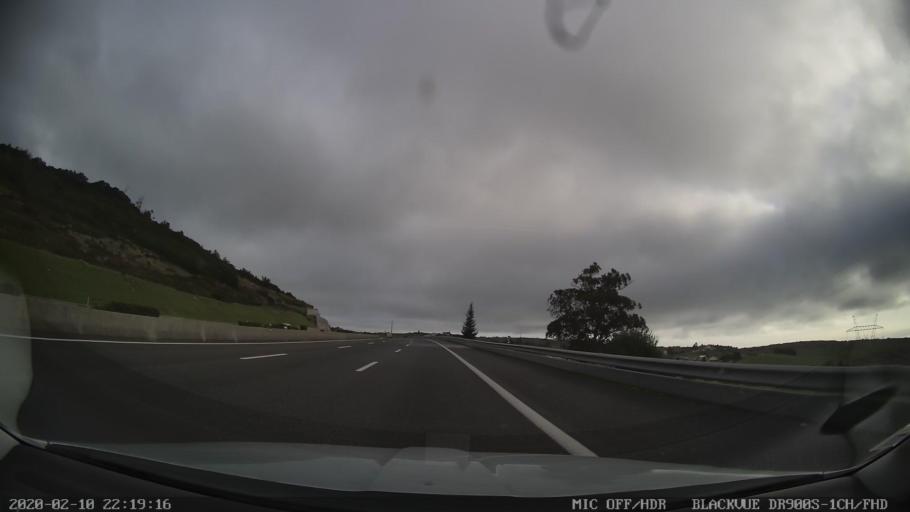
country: PT
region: Lisbon
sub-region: Arruda Dos Vinhos
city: Arruda dos Vinhos
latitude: 38.9530
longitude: -9.0643
